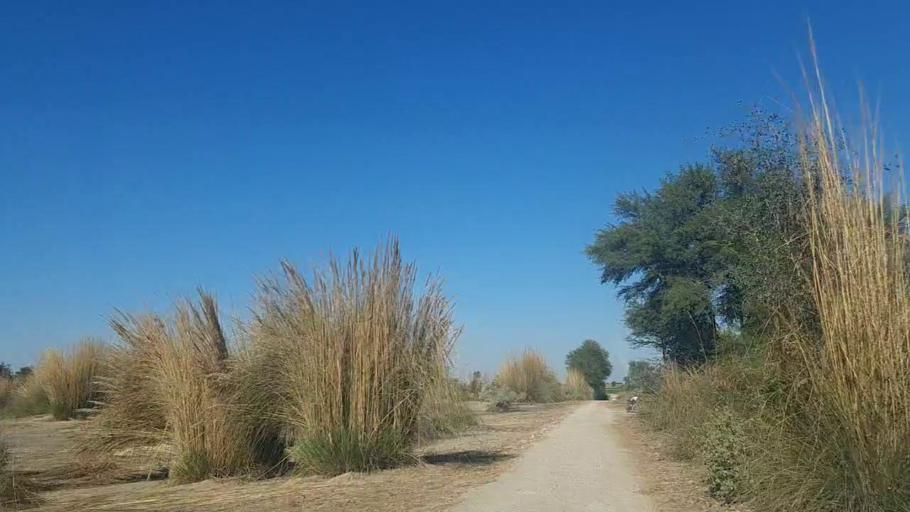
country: PK
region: Sindh
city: Khadro
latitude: 26.2183
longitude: 68.8591
